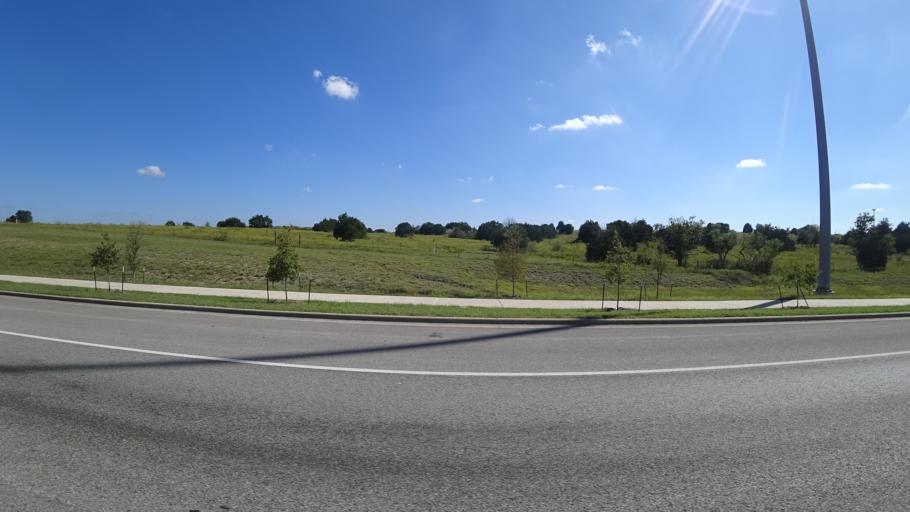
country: US
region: Texas
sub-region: Travis County
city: Manor
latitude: 30.3380
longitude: -97.5963
